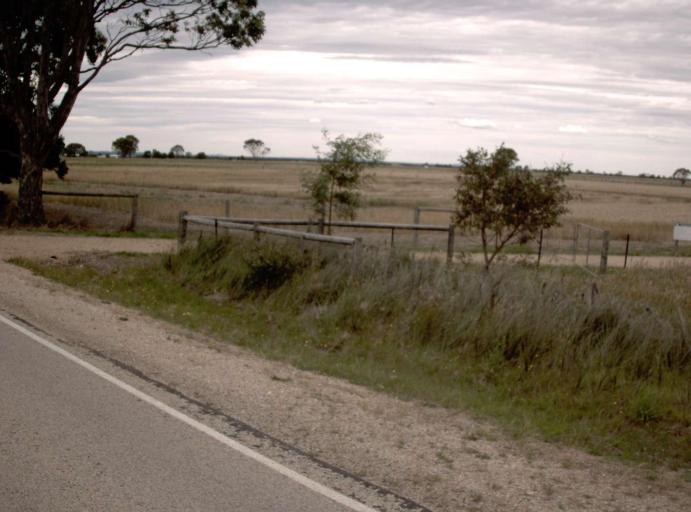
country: AU
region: Victoria
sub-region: East Gippsland
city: Bairnsdale
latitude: -37.8932
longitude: 147.5559
